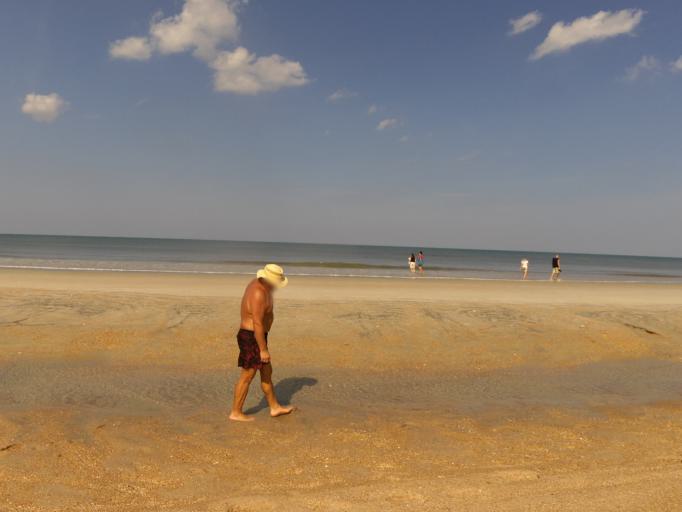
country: US
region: Florida
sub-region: Saint Johns County
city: Palm Valley
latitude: 30.1546
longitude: -81.3537
